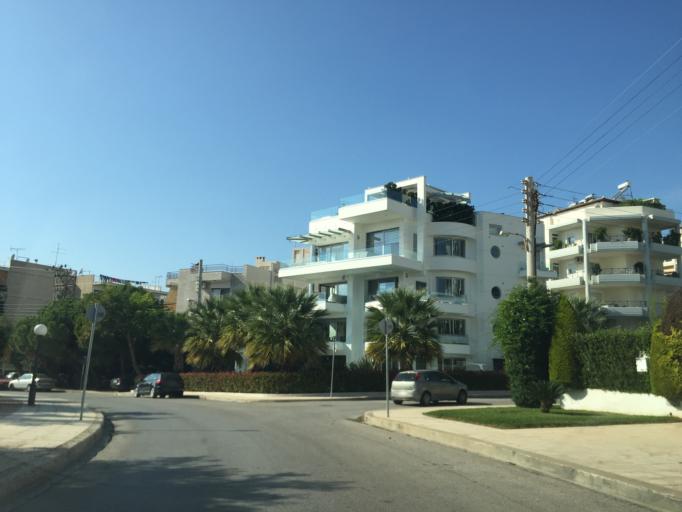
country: GR
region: Attica
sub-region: Nomarchia Anatolikis Attikis
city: Voula
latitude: 37.8469
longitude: 23.7631
